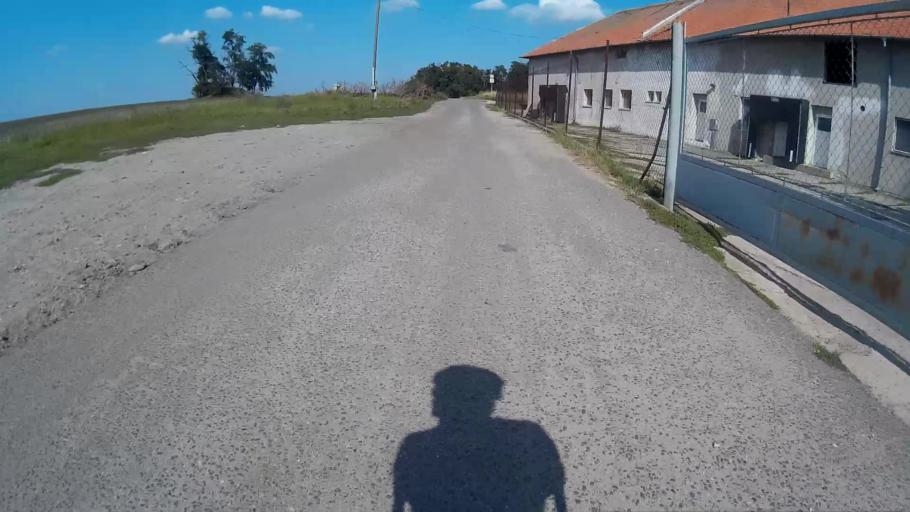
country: CZ
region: South Moravian
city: Hrusovany nad Jevisovkou
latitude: 48.7963
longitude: 16.4317
